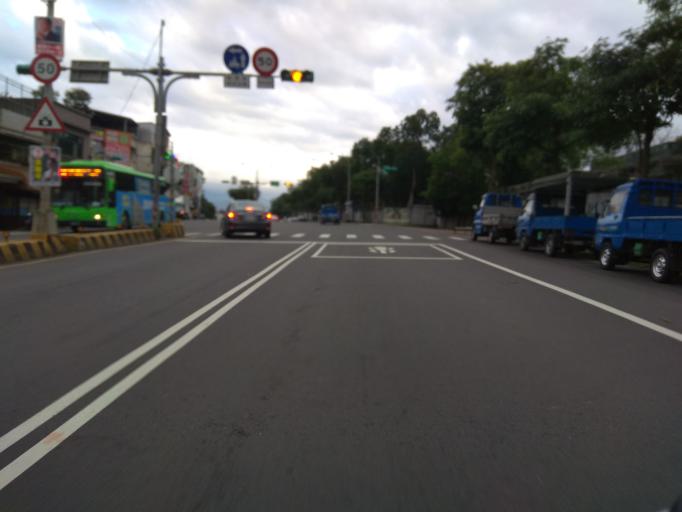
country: TW
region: Taiwan
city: Daxi
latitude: 24.8946
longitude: 121.2114
